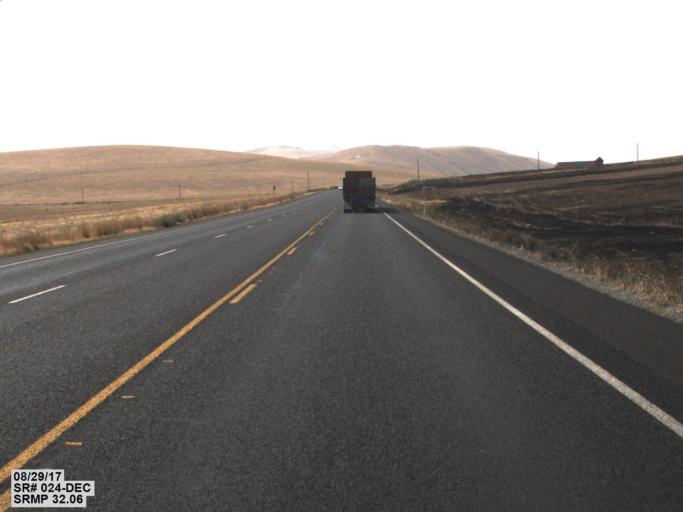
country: US
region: Washington
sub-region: Grant County
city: Desert Aire
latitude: 46.5415
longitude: -119.8489
